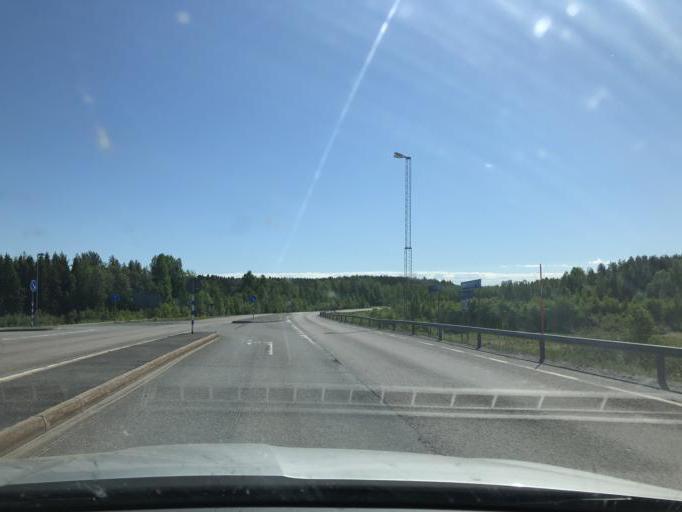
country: SE
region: Norrbotten
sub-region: Lulea Kommun
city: Bergnaset
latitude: 65.6613
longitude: 22.0979
